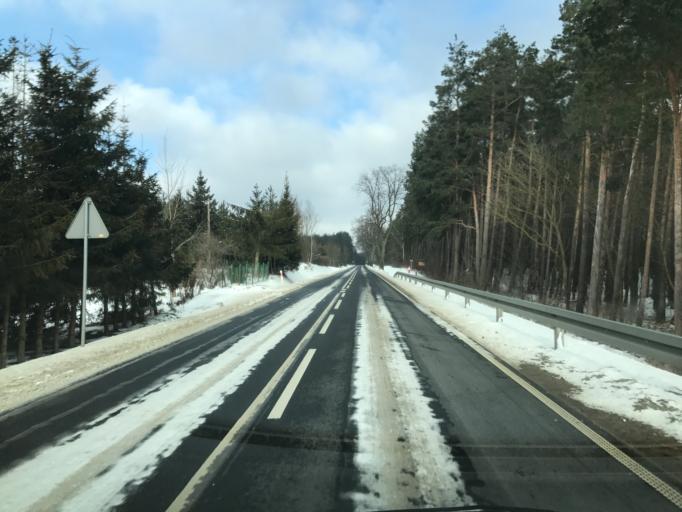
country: PL
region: Warmian-Masurian Voivodeship
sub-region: Powiat dzialdowski
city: Lidzbark
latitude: 53.3070
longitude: 19.8125
